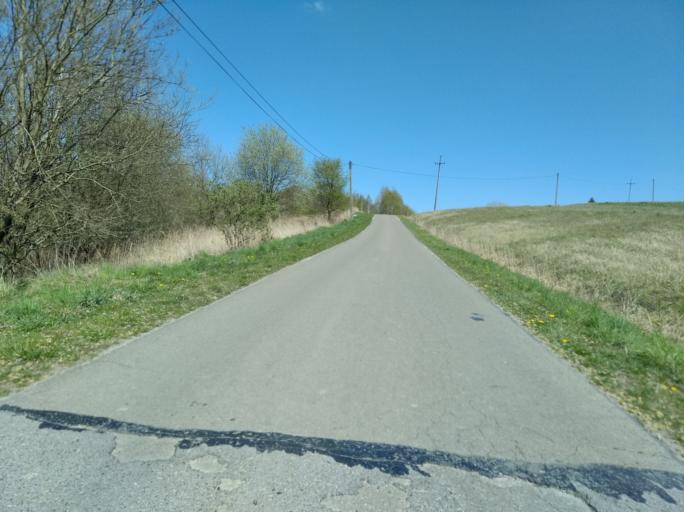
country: PL
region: Subcarpathian Voivodeship
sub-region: Powiat strzyzowski
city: Wisniowa
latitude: 49.9158
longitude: 21.6758
